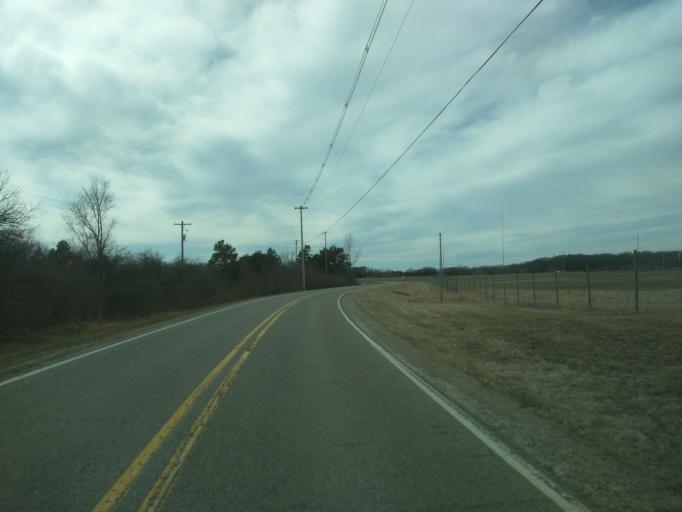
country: US
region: Michigan
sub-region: Ingham County
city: Holt
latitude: 42.6694
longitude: -84.4799
